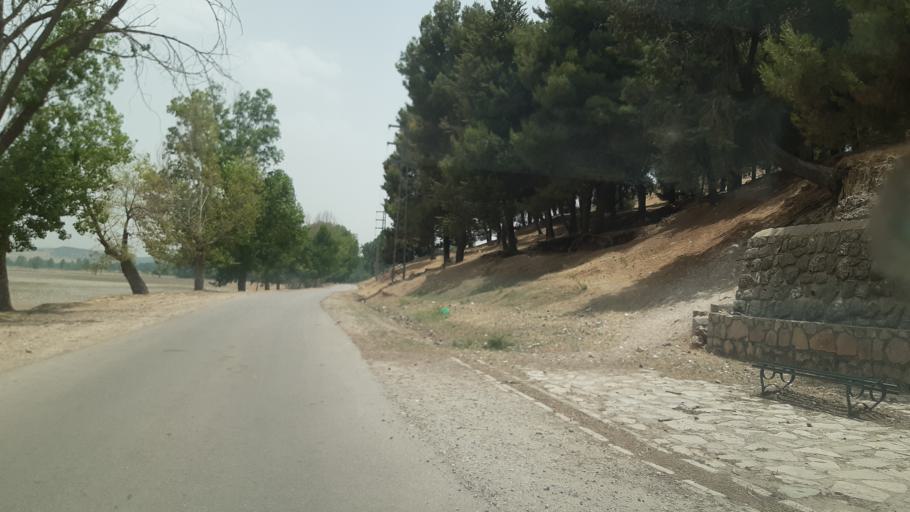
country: MA
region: Meknes-Tafilalet
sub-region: Ifrane
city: Ifrane
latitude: 33.6523
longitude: -5.0415
